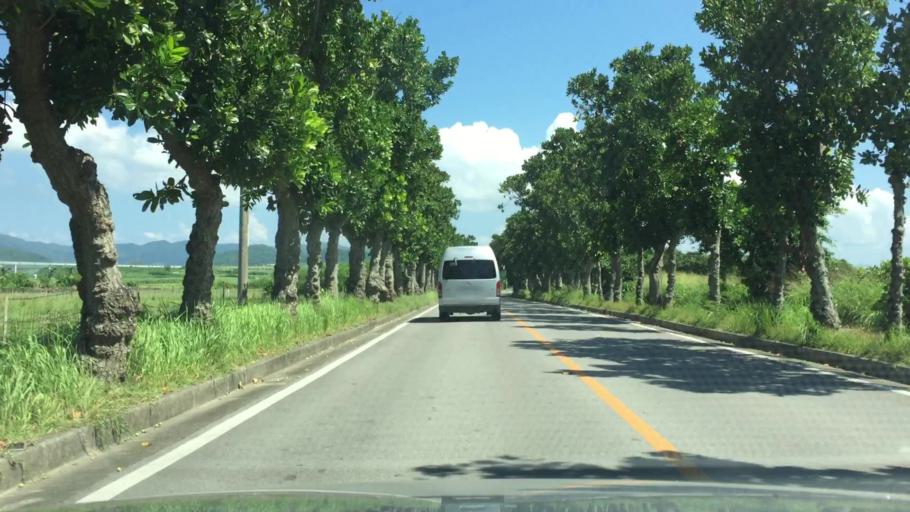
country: JP
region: Okinawa
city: Ishigaki
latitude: 24.3694
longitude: 124.2464
